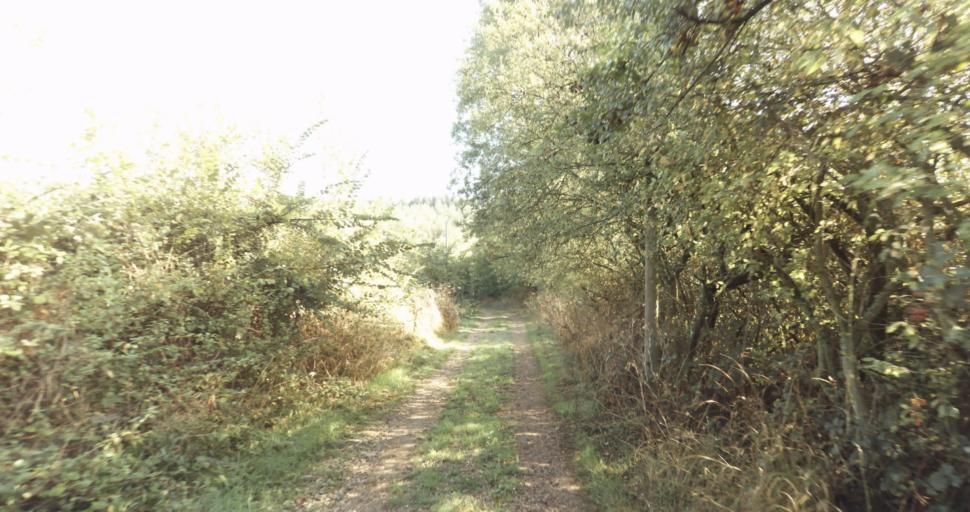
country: FR
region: Lower Normandy
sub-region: Departement de l'Orne
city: Vimoutiers
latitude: 48.9345
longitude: 0.2981
